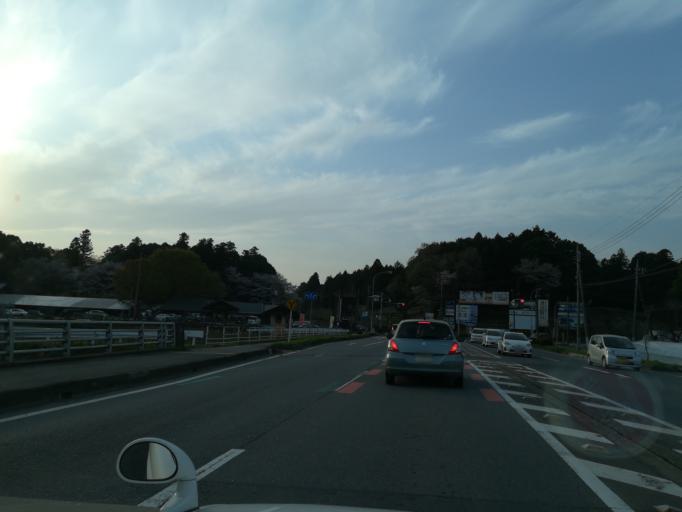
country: JP
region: Ibaraki
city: Naka
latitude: 36.0621
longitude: 140.0816
